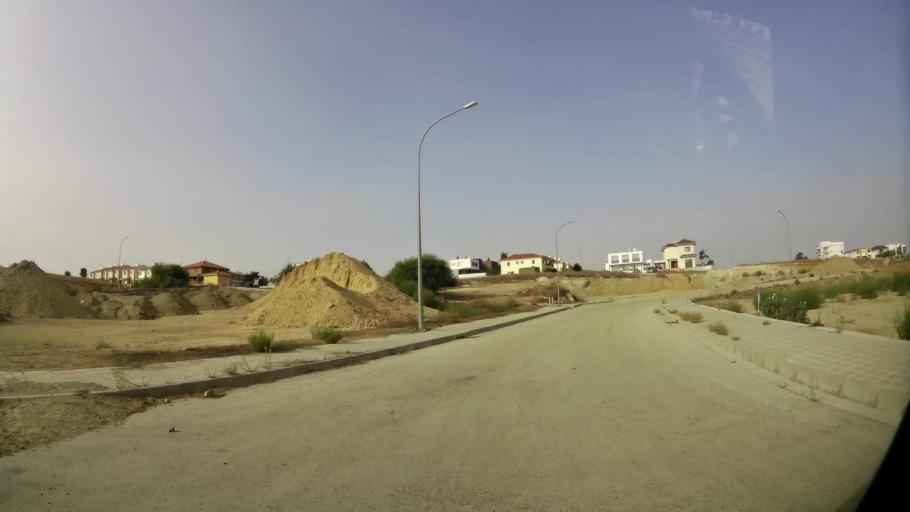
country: CY
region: Lefkosia
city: Geri
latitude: 35.0701
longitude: 33.3846
